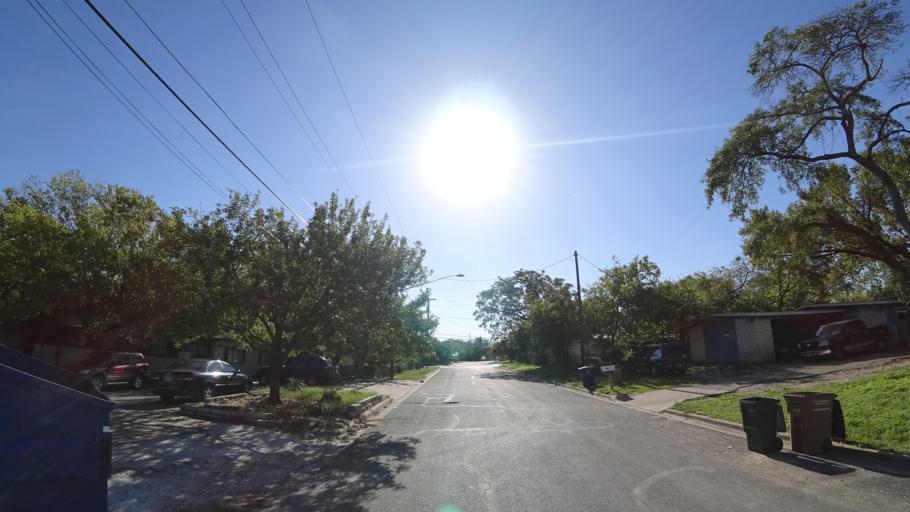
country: US
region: Texas
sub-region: Travis County
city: Austin
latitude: 30.3472
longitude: -97.7042
